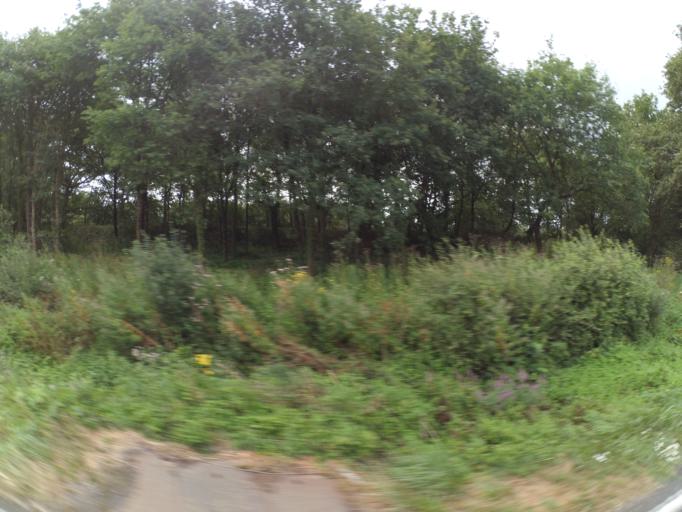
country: FR
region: Pays de la Loire
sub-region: Departement de Maine-et-Loire
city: Villedieu-la-Blouere
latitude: 47.1332
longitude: -1.0812
